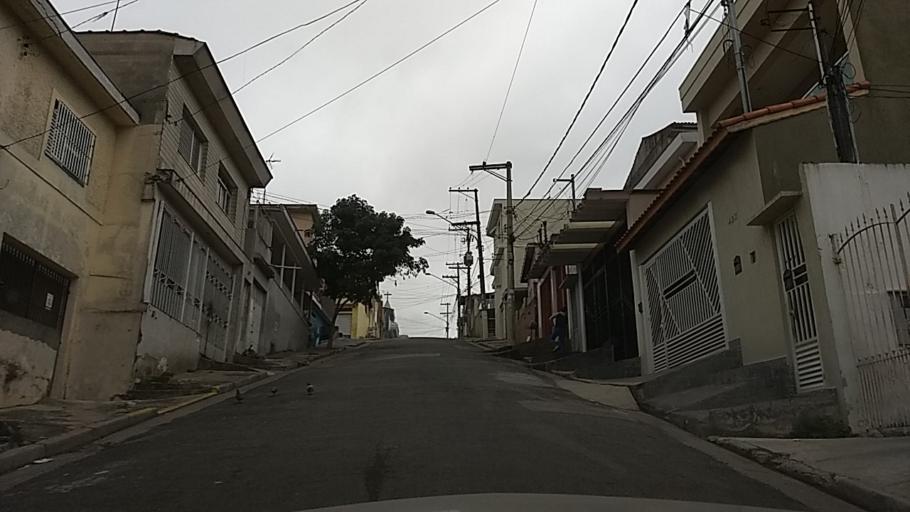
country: BR
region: Sao Paulo
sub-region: Guarulhos
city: Guarulhos
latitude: -23.4928
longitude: -46.5939
